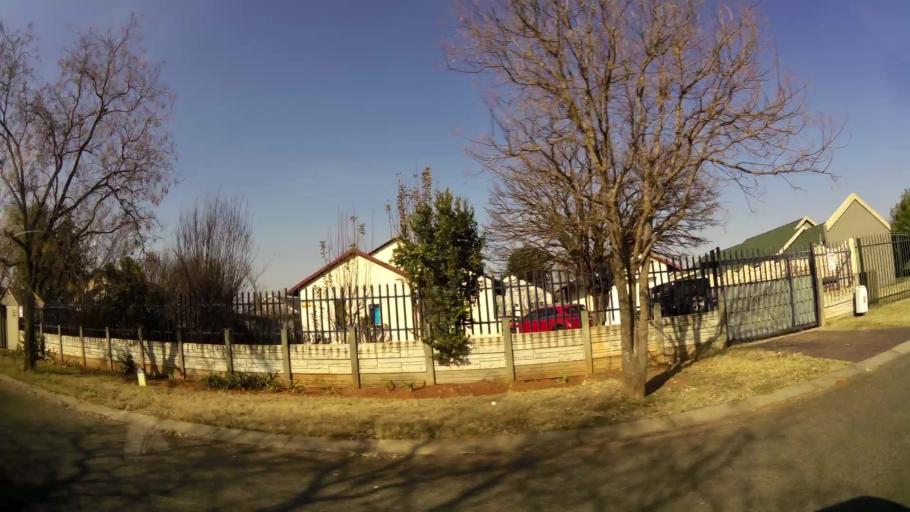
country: ZA
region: Gauteng
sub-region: West Rand District Municipality
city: Randfontein
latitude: -26.1767
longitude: 27.6892
